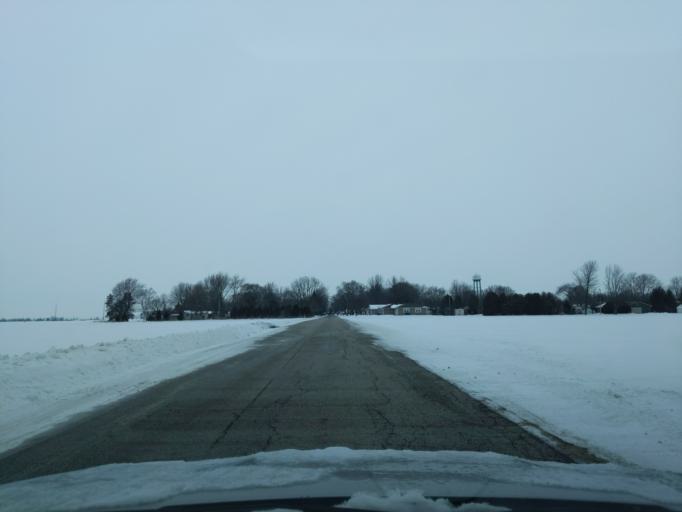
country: US
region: Indiana
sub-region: Benton County
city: Otterbein
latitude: 40.4794
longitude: -87.0934
